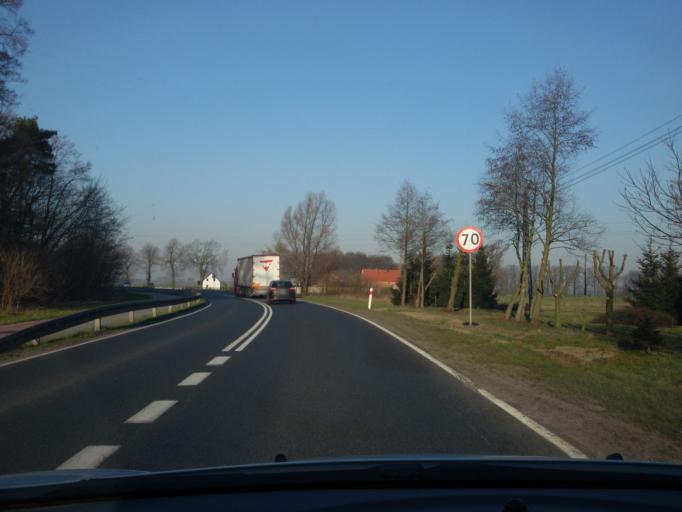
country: PL
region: Lubusz
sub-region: Powiat wschowski
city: Wschowa
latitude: 51.8198
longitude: 16.3538
